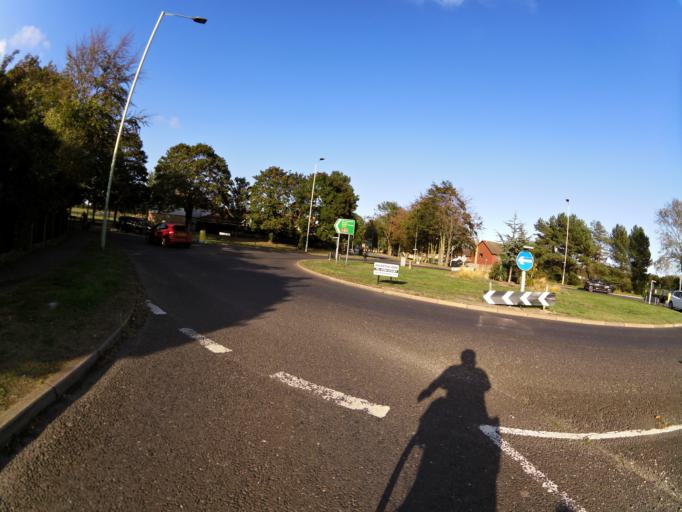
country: GB
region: England
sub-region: Suffolk
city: Kessingland
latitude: 52.4550
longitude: 1.7132
